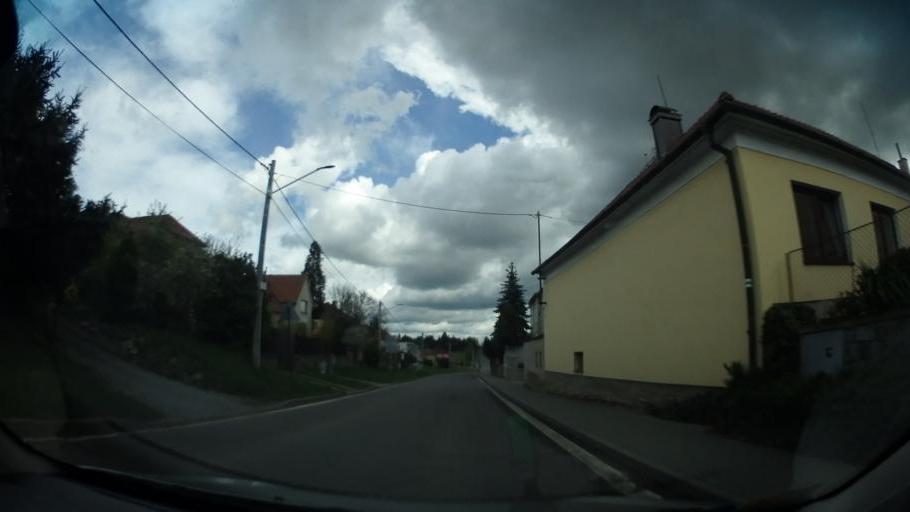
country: CZ
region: Vysocina
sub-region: Okres Zd'ar nad Sazavou
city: Velka Bites
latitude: 49.2919
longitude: 16.2266
